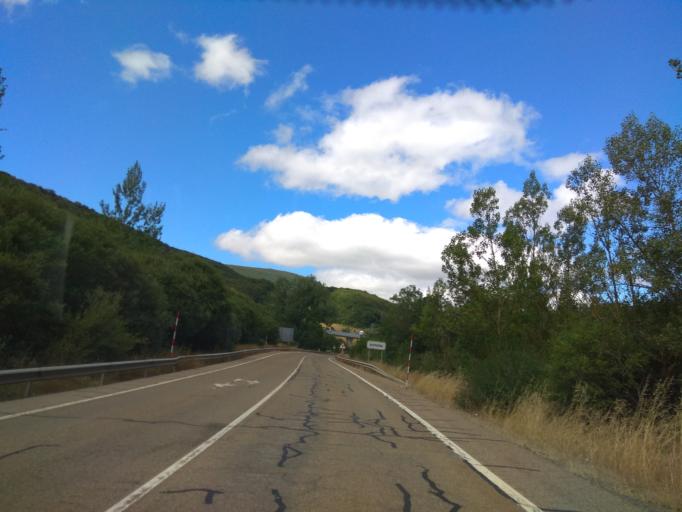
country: ES
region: Cantabria
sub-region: Provincia de Cantabria
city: Villaescusa
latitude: 42.9502
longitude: -4.1381
